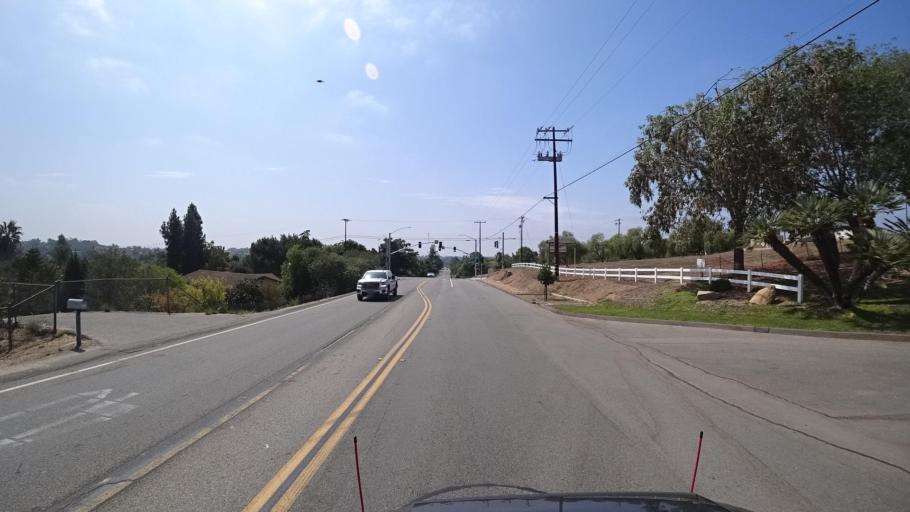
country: US
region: California
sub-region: San Diego County
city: Fallbrook
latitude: 33.3700
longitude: -117.2277
